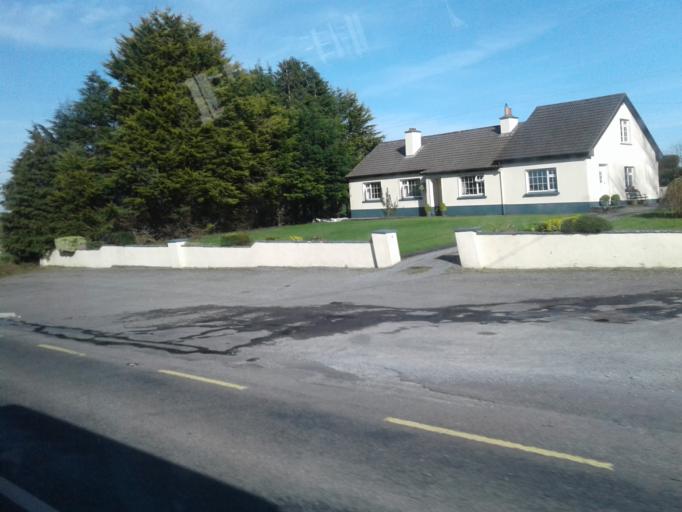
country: IE
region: Connaught
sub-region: County Galway
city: Gort
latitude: 53.0963
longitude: -8.8165
